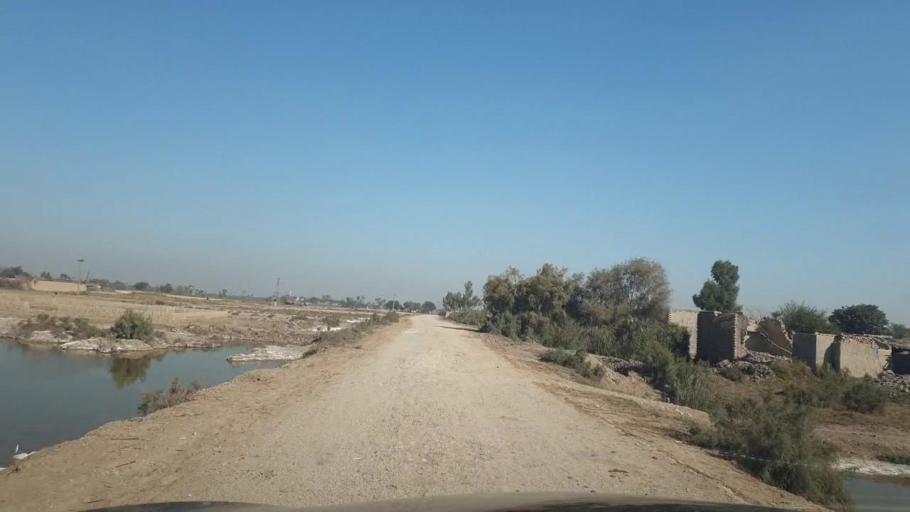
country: PK
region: Sindh
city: Ghotki
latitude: 27.9946
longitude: 69.3546
